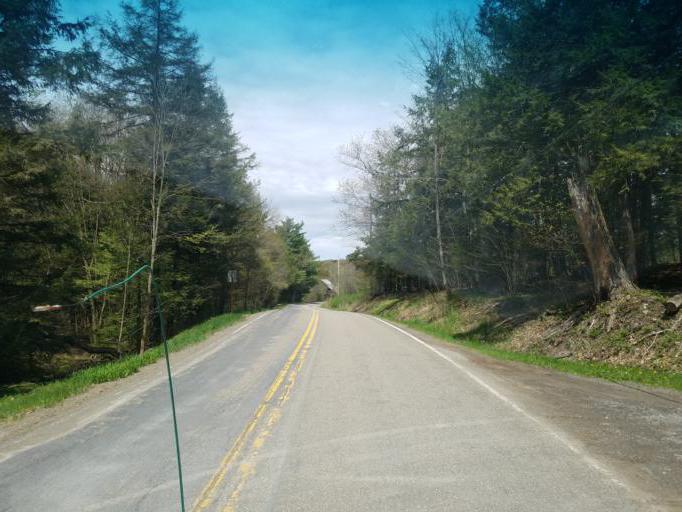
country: US
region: Pennsylvania
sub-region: Tioga County
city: Wellsboro
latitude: 41.6965
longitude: -77.4345
